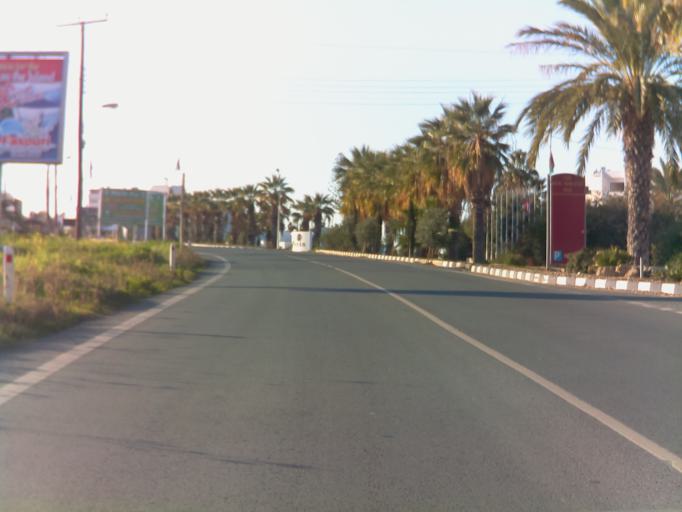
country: CY
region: Pafos
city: Kissonerga
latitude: 34.8107
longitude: 32.3962
